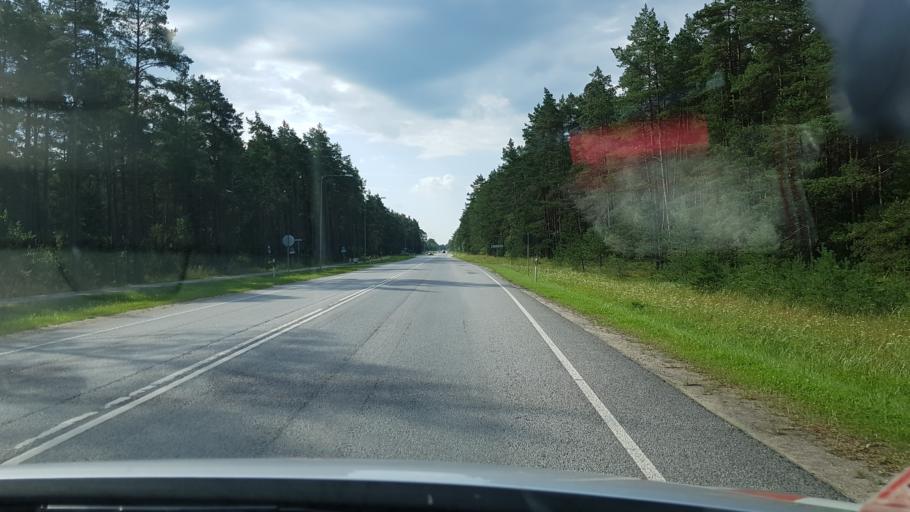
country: EE
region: Harju
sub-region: Kiili vald
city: Kiili
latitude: 59.3496
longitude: 24.7743
